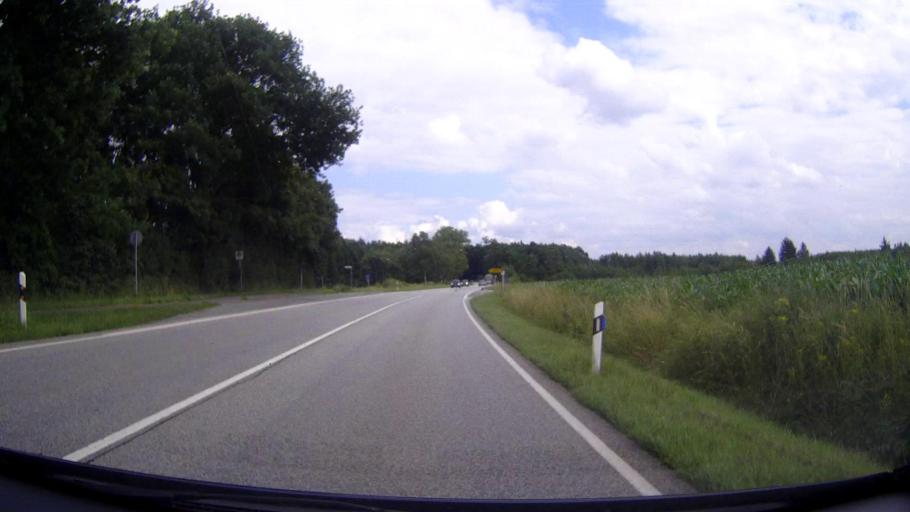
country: DE
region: Schleswig-Holstein
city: Arpsdorf
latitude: 54.0716
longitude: 9.8349
